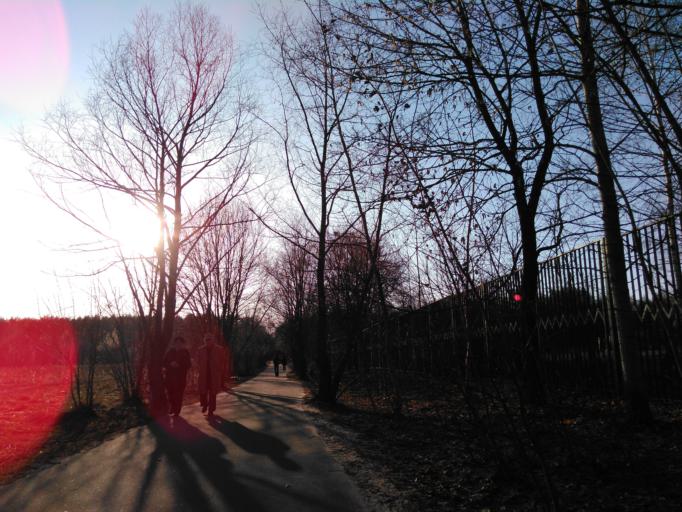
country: RU
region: Moscow
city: Zyuzino
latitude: 55.6340
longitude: 37.5819
